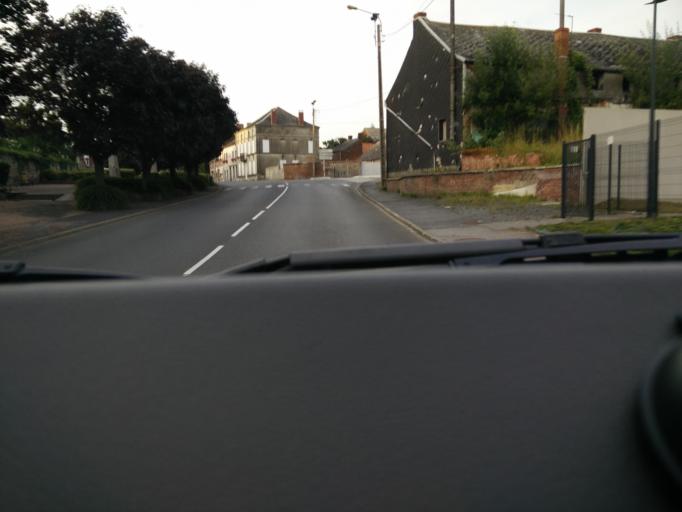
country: FR
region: Nord-Pas-de-Calais
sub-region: Departement du Nord
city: Bavay
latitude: 50.2963
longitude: 3.7970
